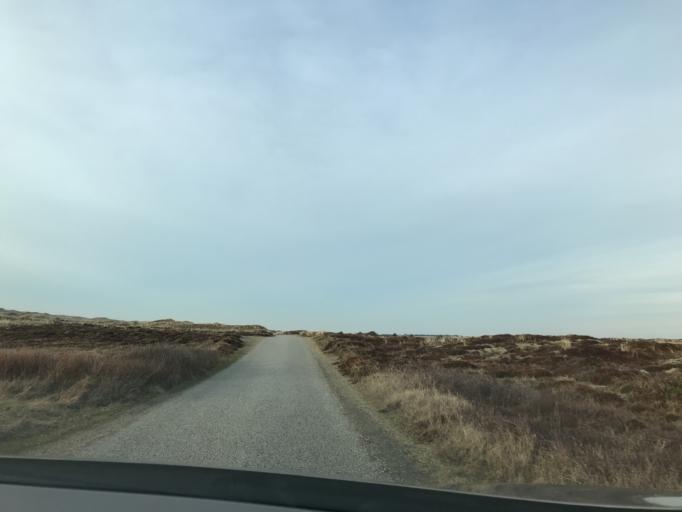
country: DK
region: South Denmark
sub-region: Varde Kommune
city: Oksbol
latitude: 55.7982
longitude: 8.1820
